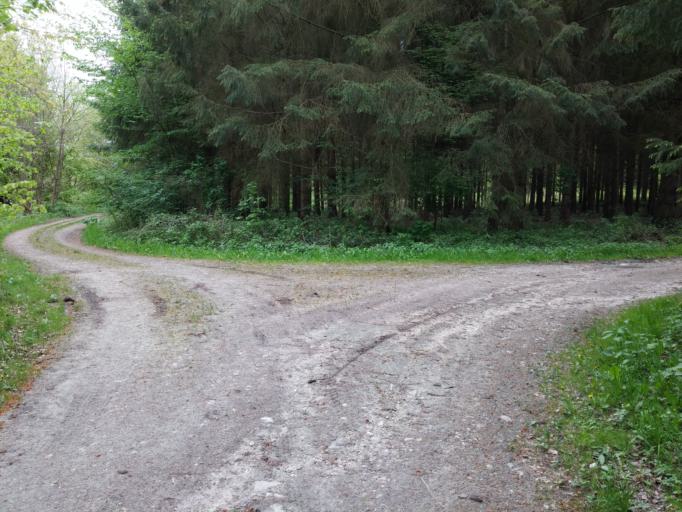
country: DK
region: South Denmark
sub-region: Kerteminde Kommune
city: Munkebo
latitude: 55.4297
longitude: 10.5617
